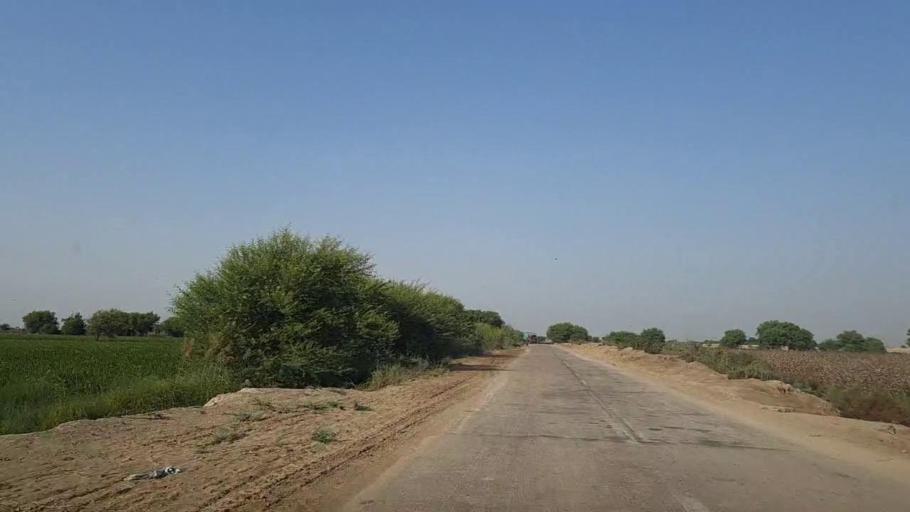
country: PK
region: Sindh
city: Mirpur Batoro
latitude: 24.5752
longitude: 68.3945
